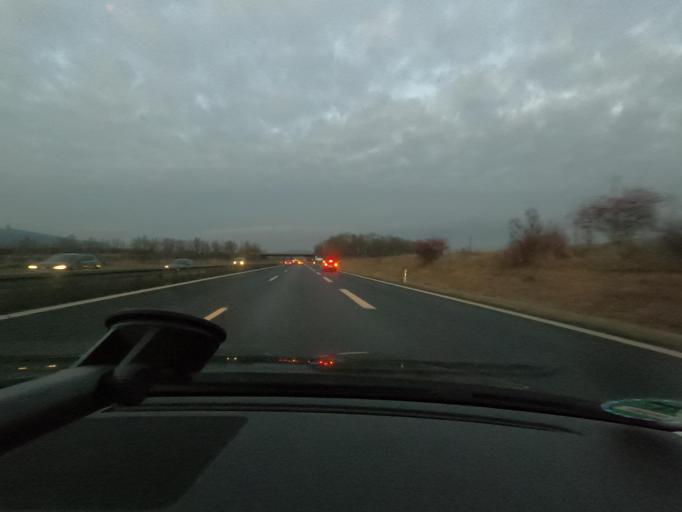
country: DE
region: Bavaria
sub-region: Upper Franconia
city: Bad Staffelstein
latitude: 50.1075
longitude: 11.0131
